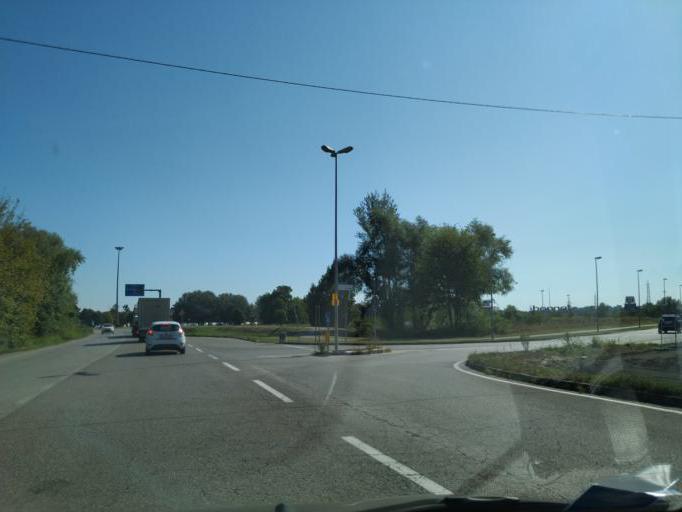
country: IT
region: Emilia-Romagna
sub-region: Provincia di Ferrara
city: Corpo Reno
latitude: 44.7484
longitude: 11.2965
